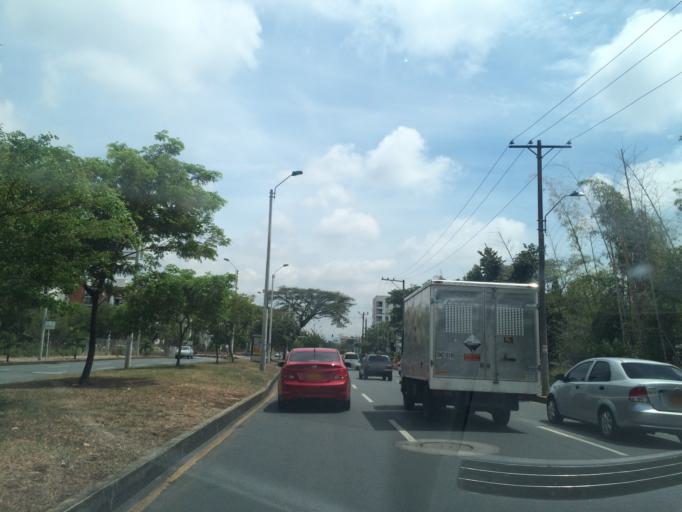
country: CO
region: Valle del Cauca
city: Cali
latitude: 3.3912
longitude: -76.5282
